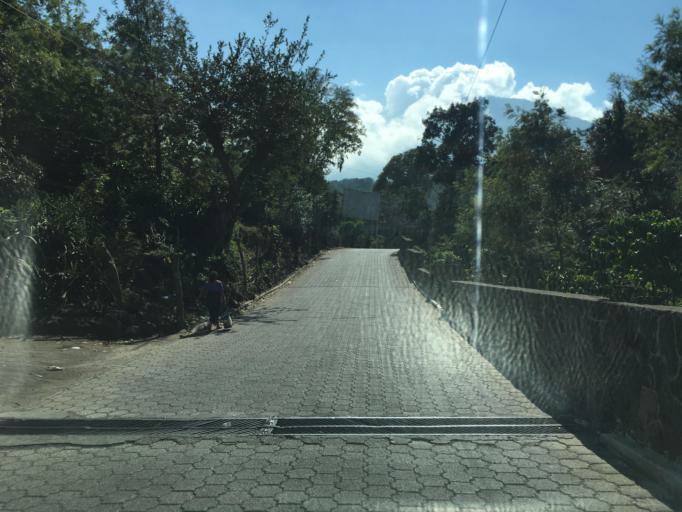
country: GT
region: Solola
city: San Antonio Palopo
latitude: 14.6647
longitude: -91.1636
